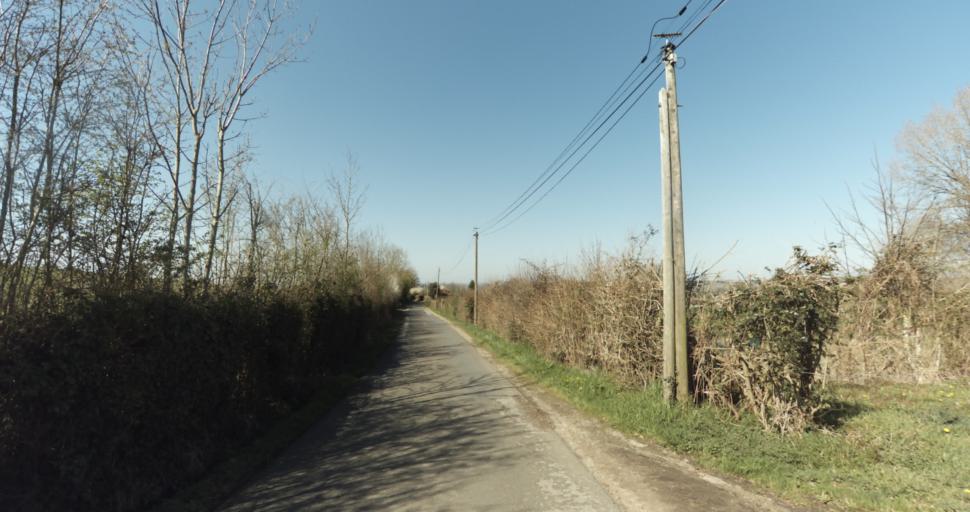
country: FR
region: Lower Normandy
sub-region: Departement du Calvados
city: Saint-Pierre-sur-Dives
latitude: 49.0174
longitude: 0.0505
